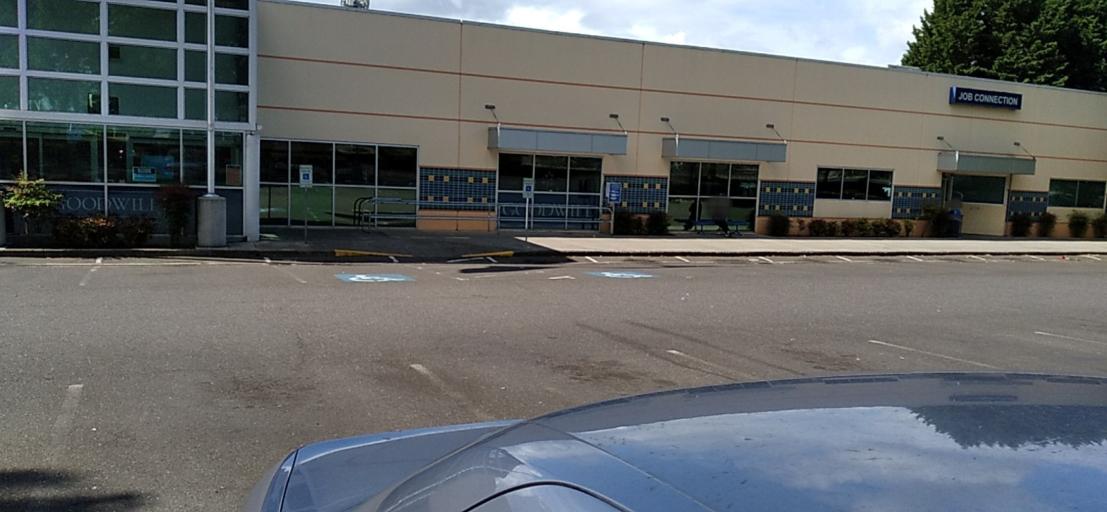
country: US
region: Washington
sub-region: Clark County
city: Walnut Grove
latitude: 45.6437
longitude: -122.6055
